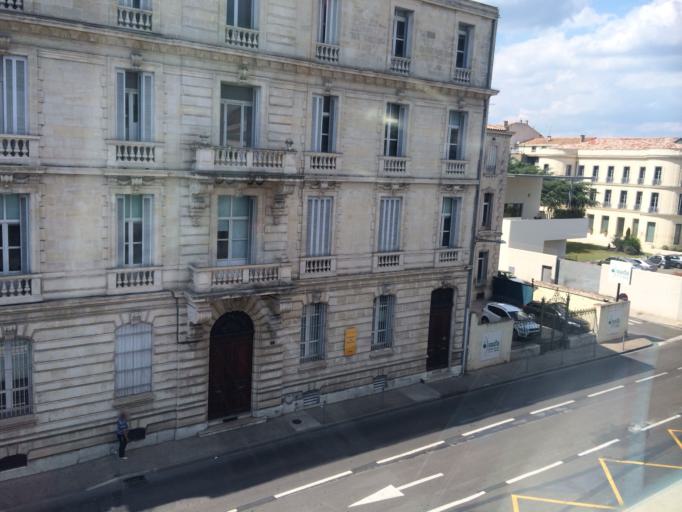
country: FR
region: Languedoc-Roussillon
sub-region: Departement du Gard
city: Nimes
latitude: 43.8314
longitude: 4.3649
